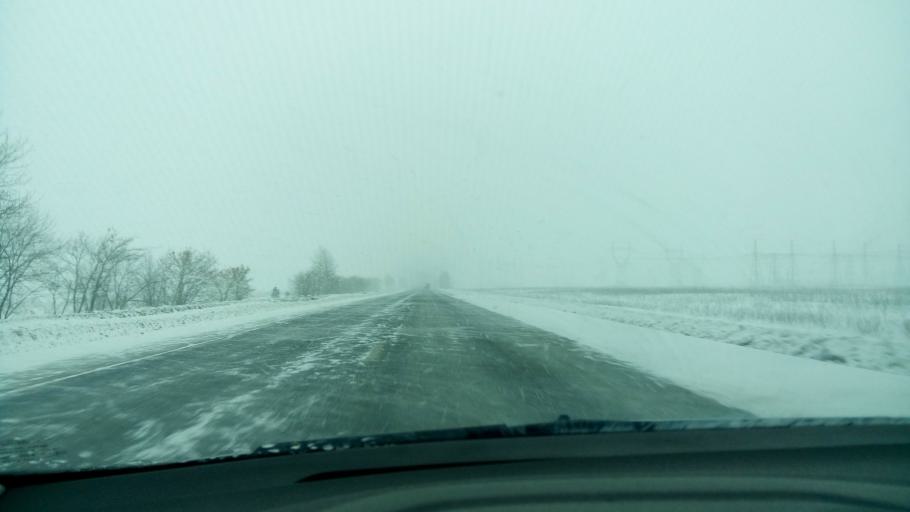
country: RU
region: Sverdlovsk
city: Beloyarskiy
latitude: 56.7733
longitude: 61.5050
